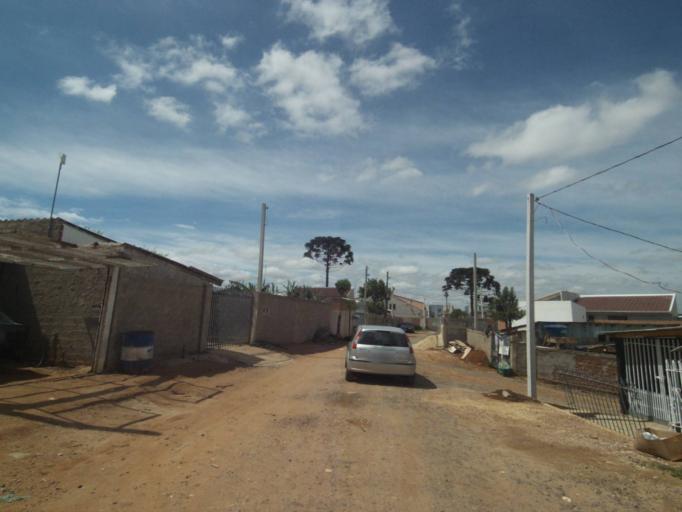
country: BR
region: Parana
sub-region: Curitiba
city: Curitiba
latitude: -25.4913
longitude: -49.3386
